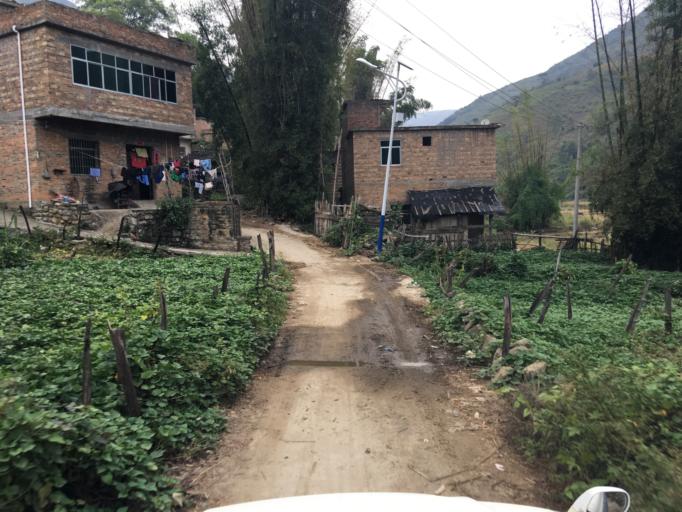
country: CN
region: Guangxi Zhuangzu Zizhiqu
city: Leli
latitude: 24.7675
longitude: 106.0920
